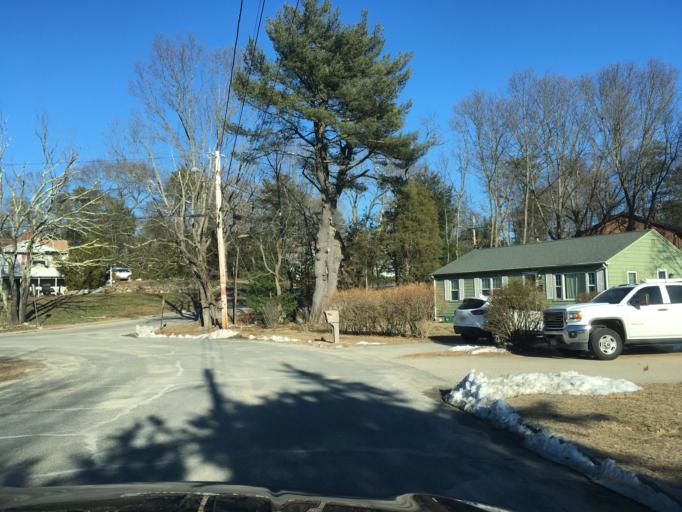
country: US
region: Rhode Island
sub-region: Kent County
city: East Greenwich
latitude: 41.6392
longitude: -71.4667
